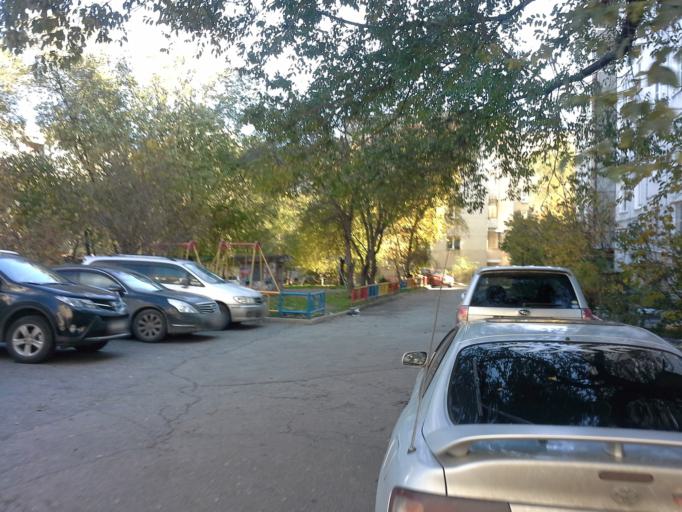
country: RU
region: Khabarovsk Krai
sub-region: Khabarovskiy Rayon
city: Khabarovsk
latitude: 48.4680
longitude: 135.0687
